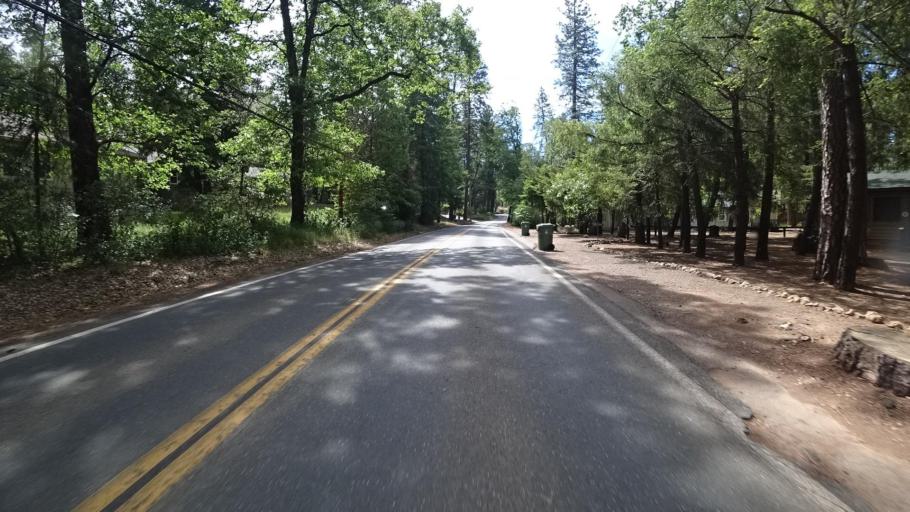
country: US
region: California
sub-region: Lake County
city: Cobb
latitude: 38.8621
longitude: -122.7150
